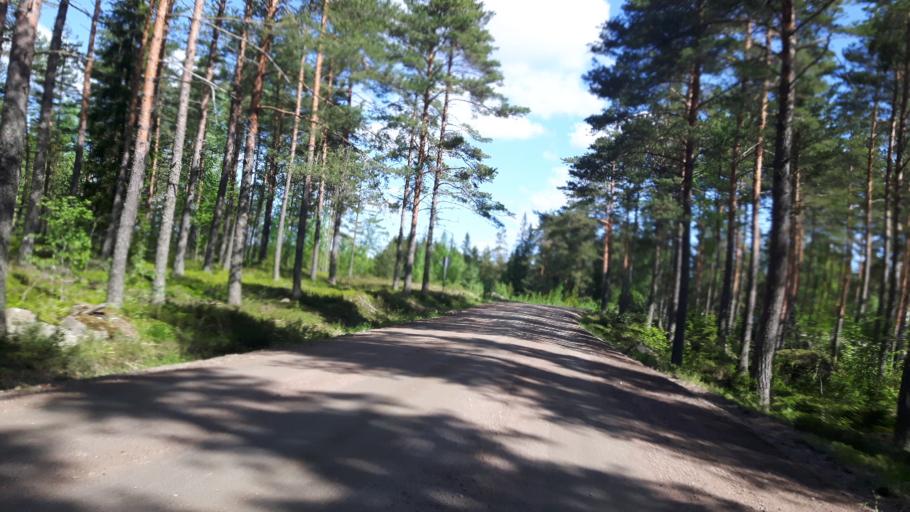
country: FI
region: Kymenlaakso
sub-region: Kotka-Hamina
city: Hamina
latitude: 60.5308
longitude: 27.2858
